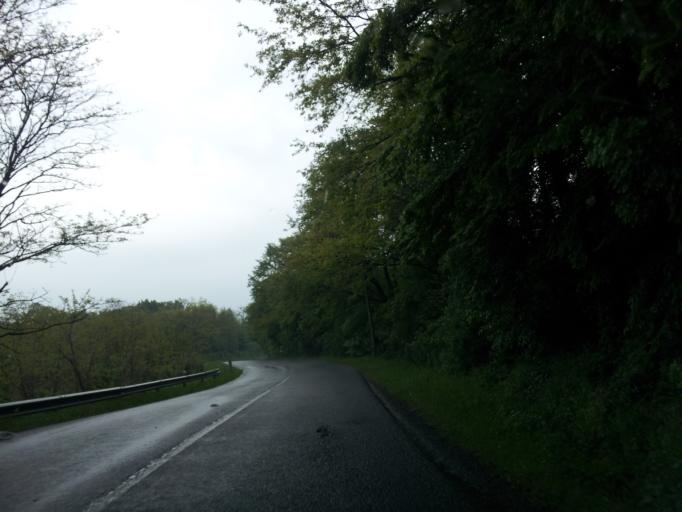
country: HU
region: Baranya
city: Hosszuheteny
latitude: 46.1798
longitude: 18.3188
